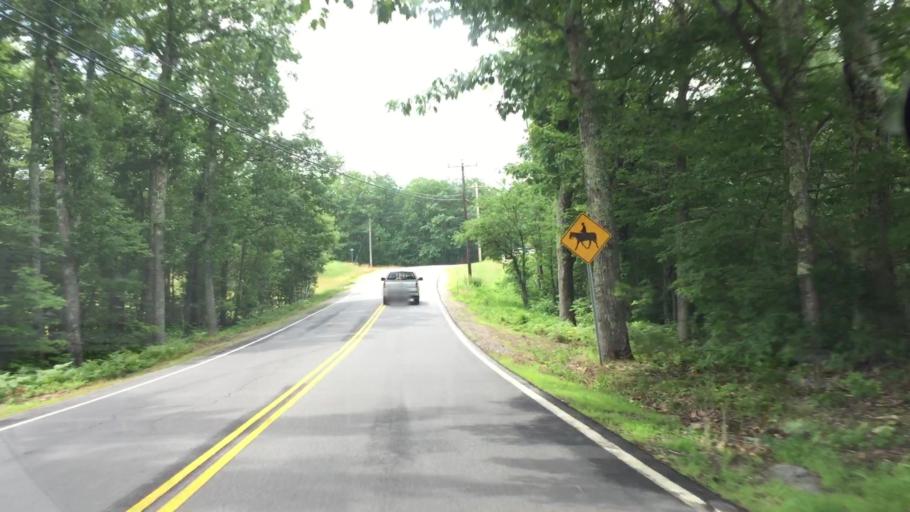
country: US
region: New Hampshire
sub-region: Grafton County
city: Holderness
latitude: 43.7673
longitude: -71.5547
